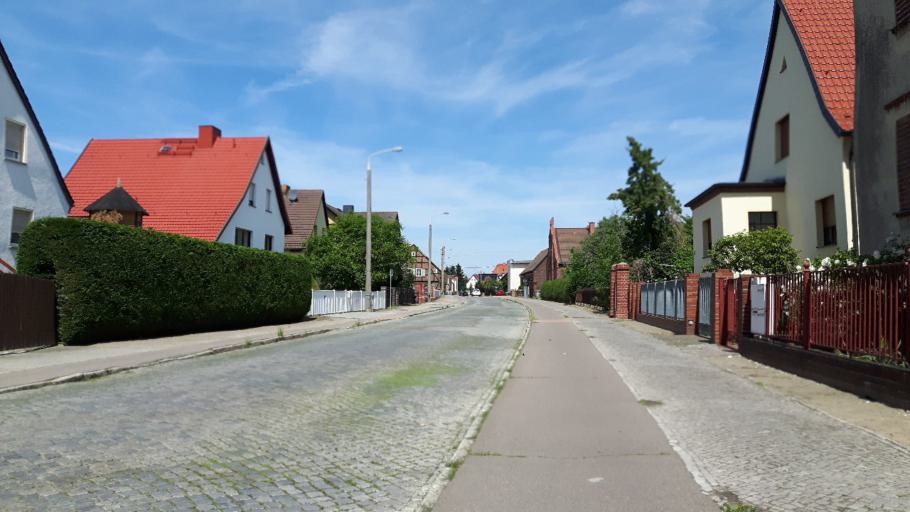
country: DE
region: Saxony-Anhalt
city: Wittenburg
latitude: 51.9018
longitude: 12.6431
